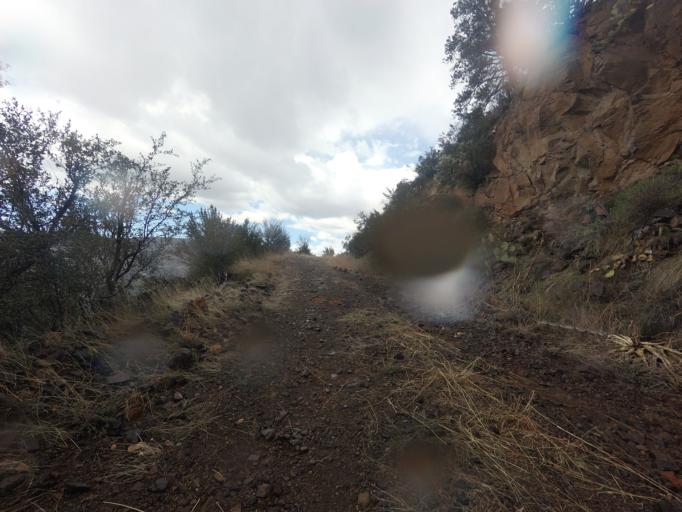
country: US
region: Arizona
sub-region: Gila County
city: Pine
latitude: 34.4039
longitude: -111.5937
